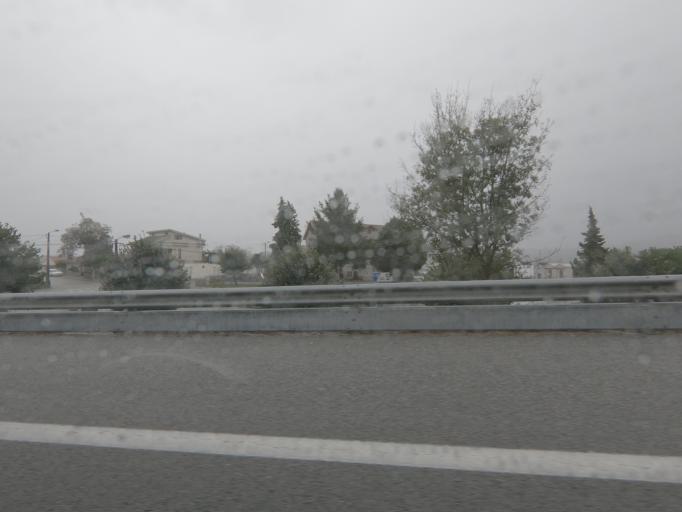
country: PT
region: Porto
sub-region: Lousada
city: Meinedo
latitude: 41.2317
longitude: -8.2106
